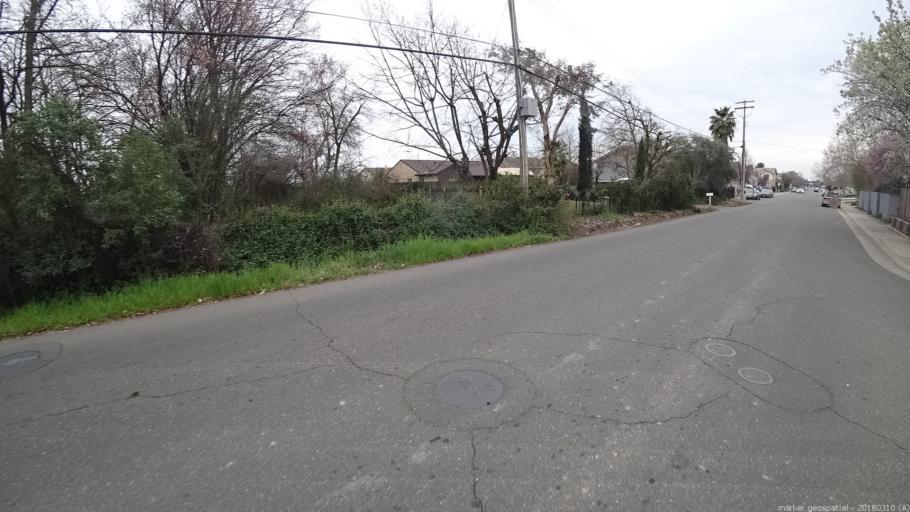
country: US
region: California
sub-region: Sacramento County
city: Vineyard
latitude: 38.4561
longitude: -121.3662
